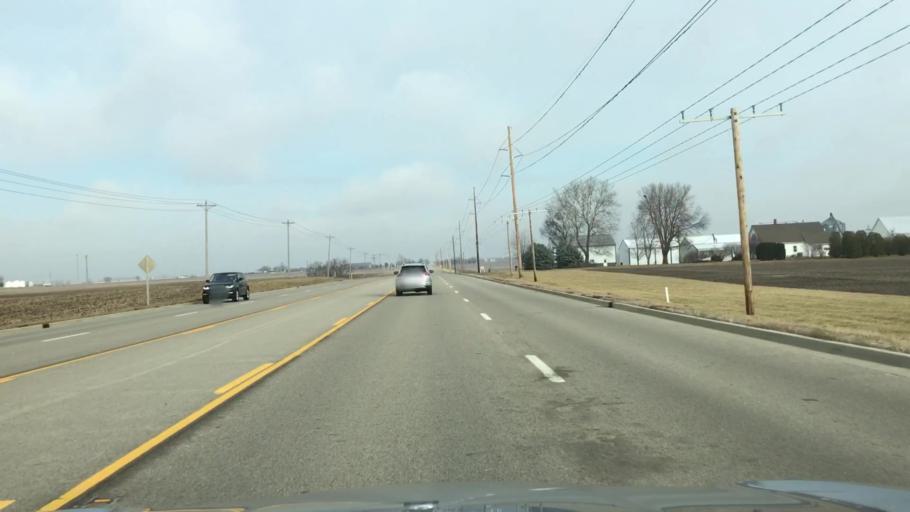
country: US
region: Illinois
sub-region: McLean County
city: Normal
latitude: 40.5190
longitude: -88.9029
